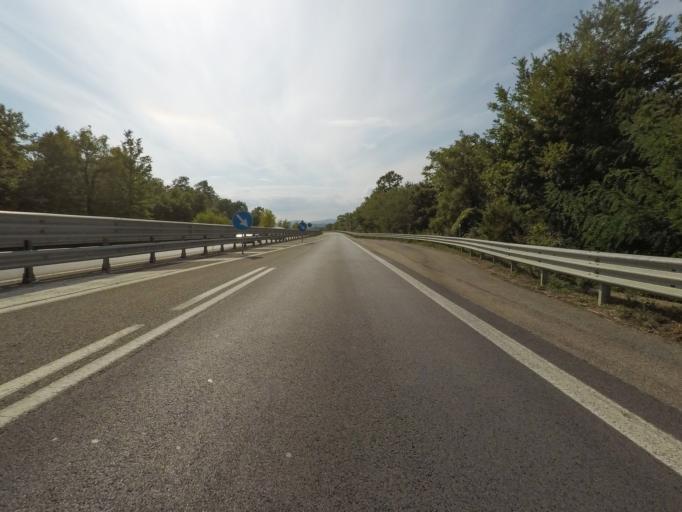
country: IT
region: Tuscany
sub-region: Provincia di Siena
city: Rosia
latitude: 43.2252
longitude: 11.2741
